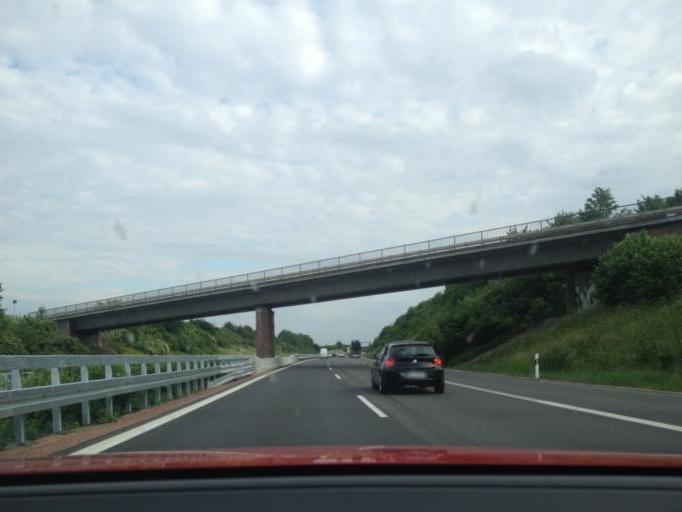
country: DE
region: Saxony-Anhalt
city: Oppin
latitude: 51.5562
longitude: 12.0053
